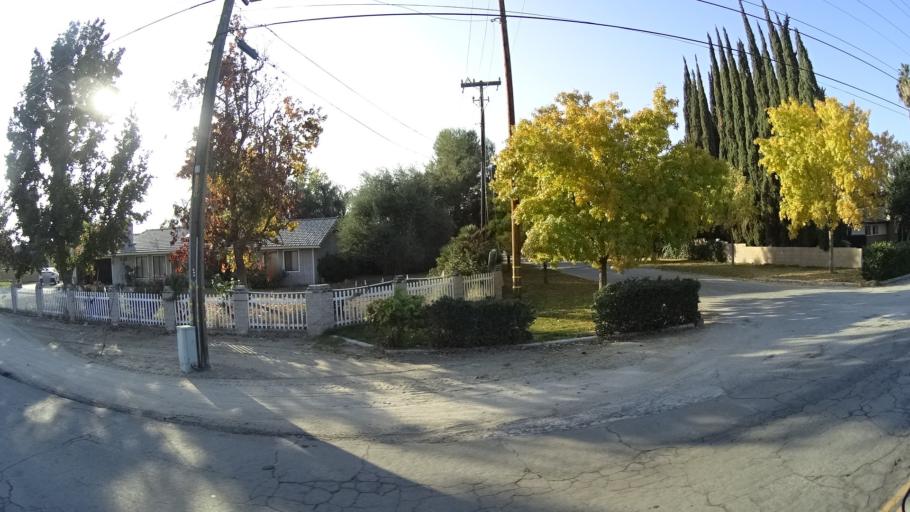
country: US
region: California
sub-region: Kern County
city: Rosedale
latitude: 35.3879
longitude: -119.1544
